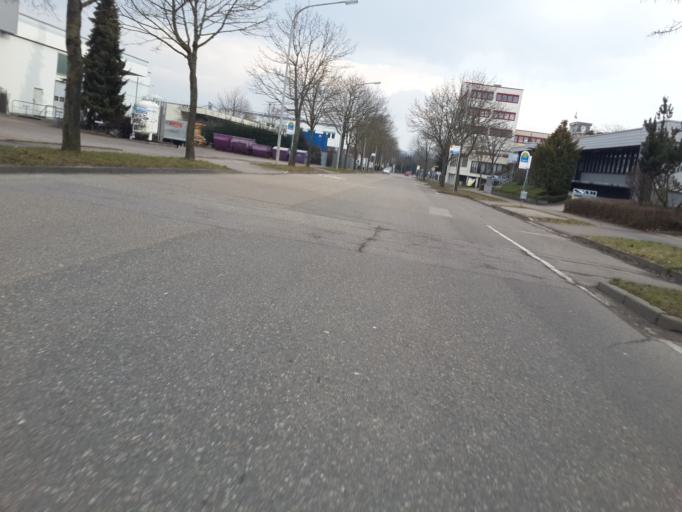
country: DE
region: Baden-Wuerttemberg
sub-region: Regierungsbezirk Stuttgart
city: Untereisesheim
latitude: 49.1850
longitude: 9.1795
